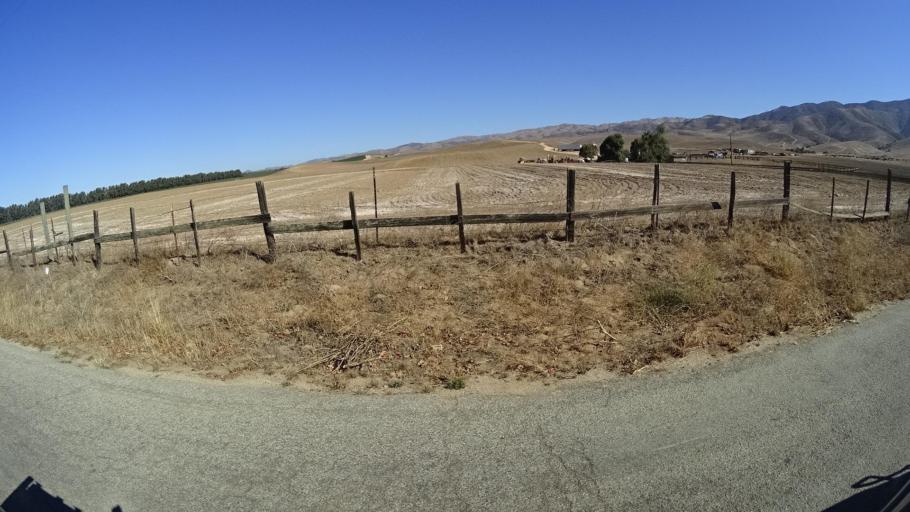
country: US
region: California
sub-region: Monterey County
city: Soledad
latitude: 36.4814
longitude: -121.3543
